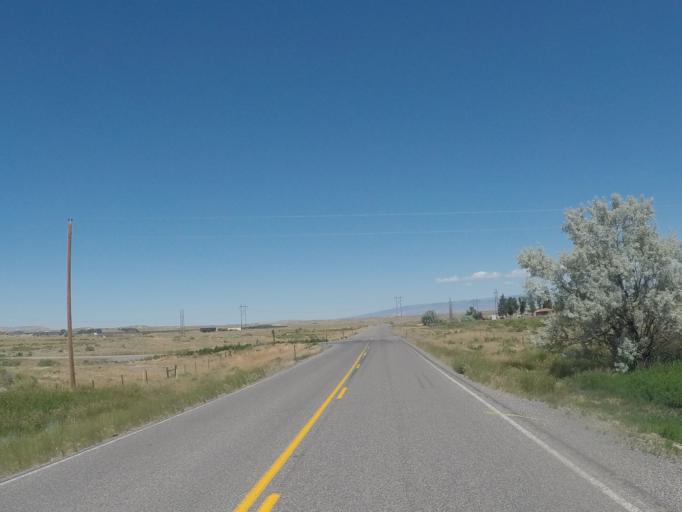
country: US
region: Wyoming
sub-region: Park County
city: Powell
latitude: 44.7300
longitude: -108.5872
